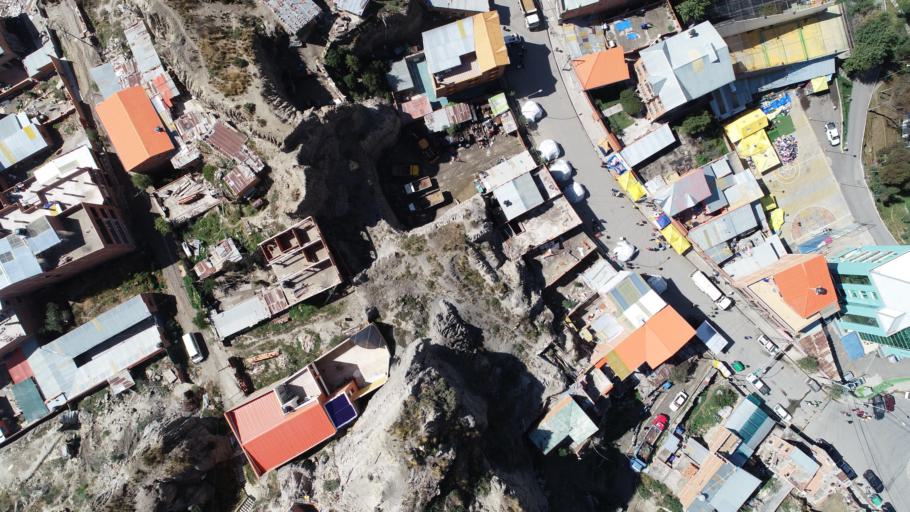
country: BO
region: La Paz
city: La Paz
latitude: -16.5194
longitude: -68.1247
